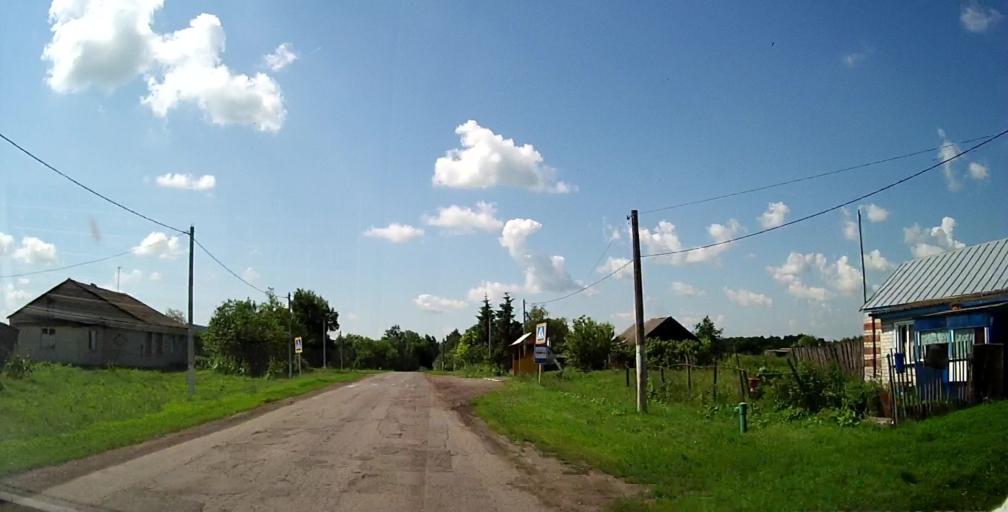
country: RU
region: Lipetsk
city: Chaplygin
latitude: 53.3735
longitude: 39.9171
